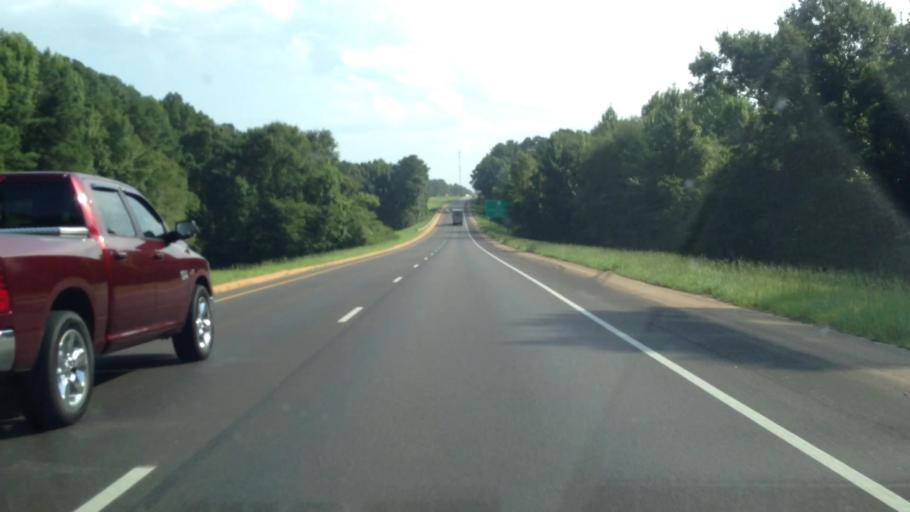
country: US
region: Mississippi
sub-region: Copiah County
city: Crystal Springs
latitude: 32.0051
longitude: -90.3663
